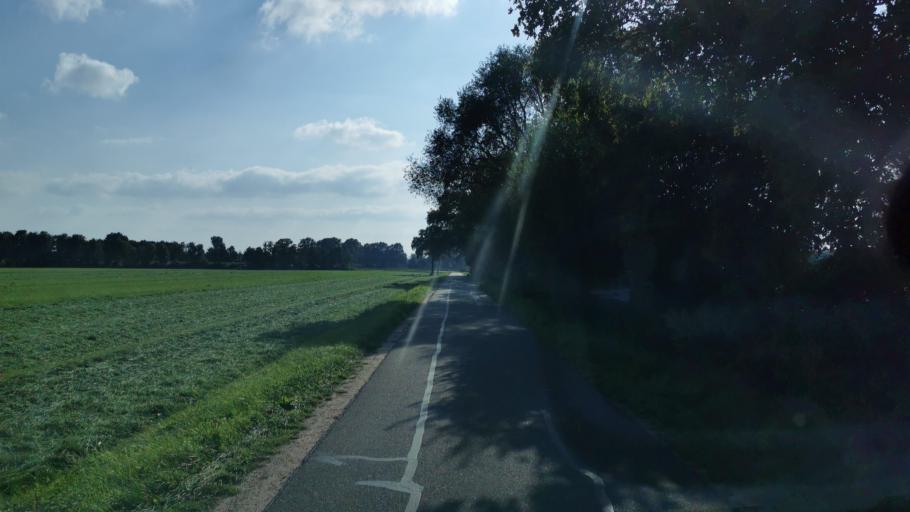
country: NL
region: Overijssel
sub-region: Gemeente Borne
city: Borne
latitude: 52.3416
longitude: 6.7675
